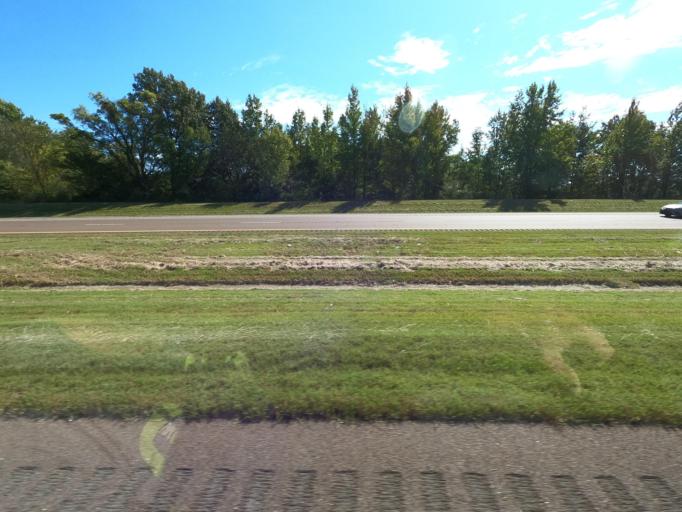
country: US
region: Tennessee
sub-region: Dyer County
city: Dyersburg
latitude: 36.0693
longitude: -89.3539
